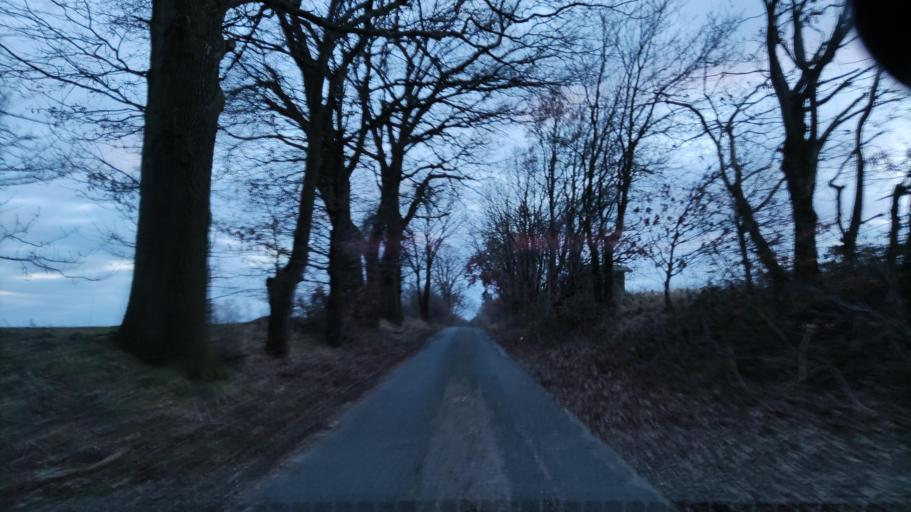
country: DE
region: Lower Saxony
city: Natendorf
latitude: 53.0714
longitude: 10.4291
